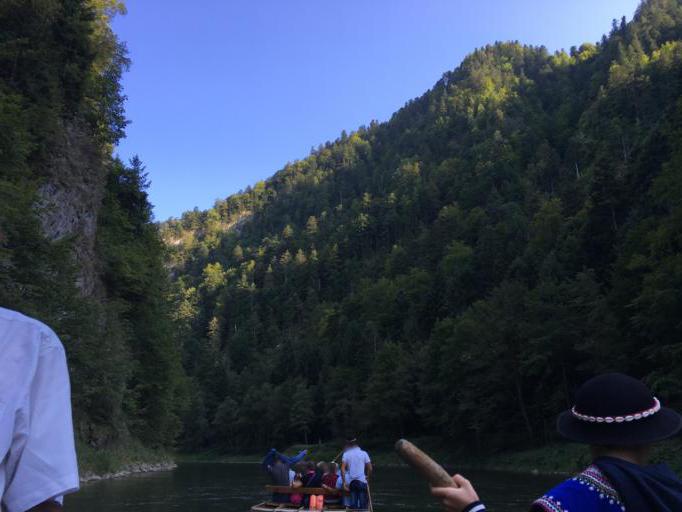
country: PL
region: Lesser Poland Voivodeship
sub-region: Powiat nowotarski
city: Kroscienko nad Dunajcem
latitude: 49.4132
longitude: 20.4440
